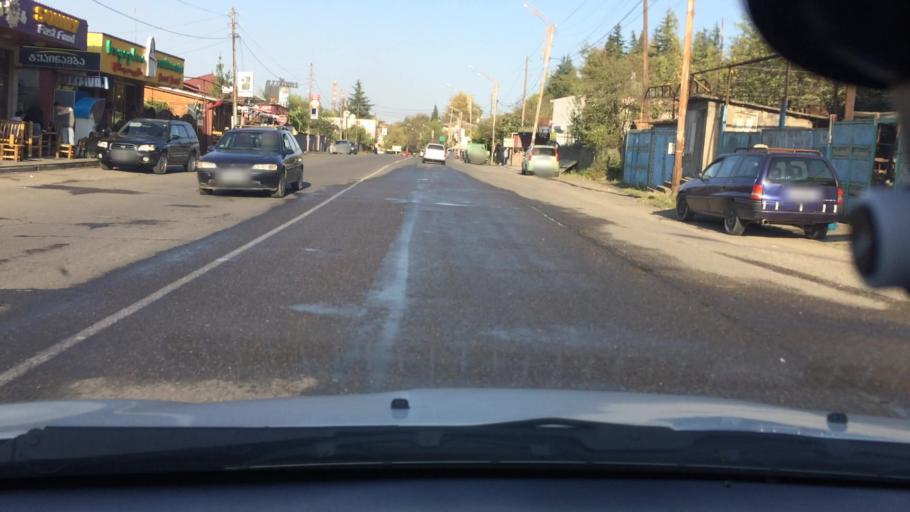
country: GE
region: Imereti
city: Zestap'oni
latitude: 42.1128
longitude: 43.0370
